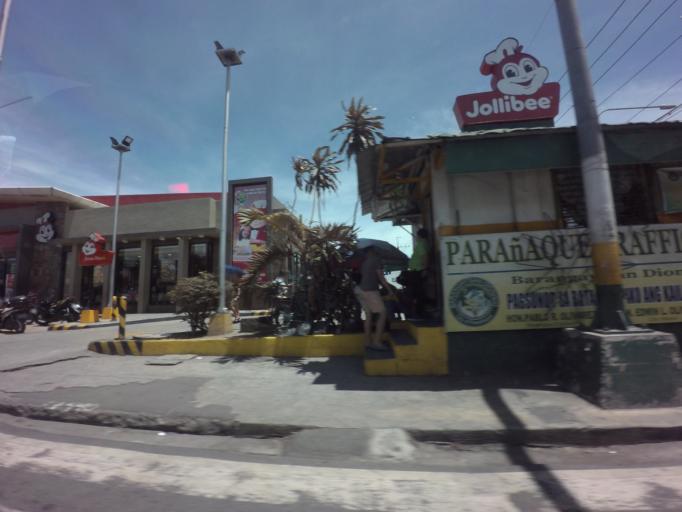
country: PH
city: Sambayanihan People's Village
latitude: 14.4920
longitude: 120.9880
